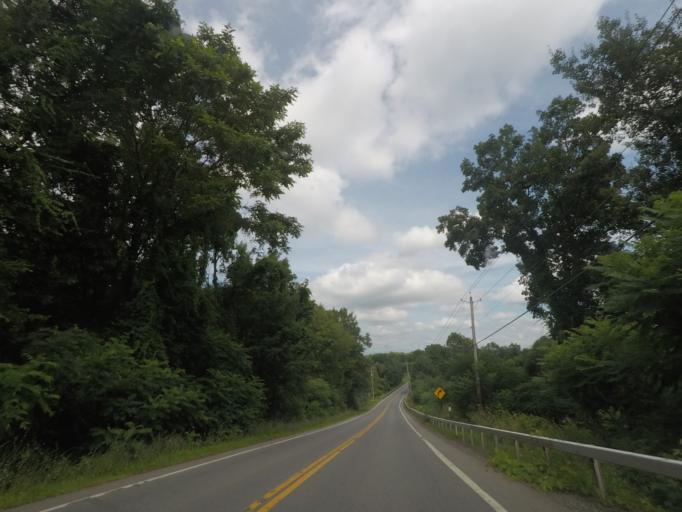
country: US
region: New York
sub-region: Saratoga County
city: Stillwater
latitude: 43.0240
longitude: -73.6798
